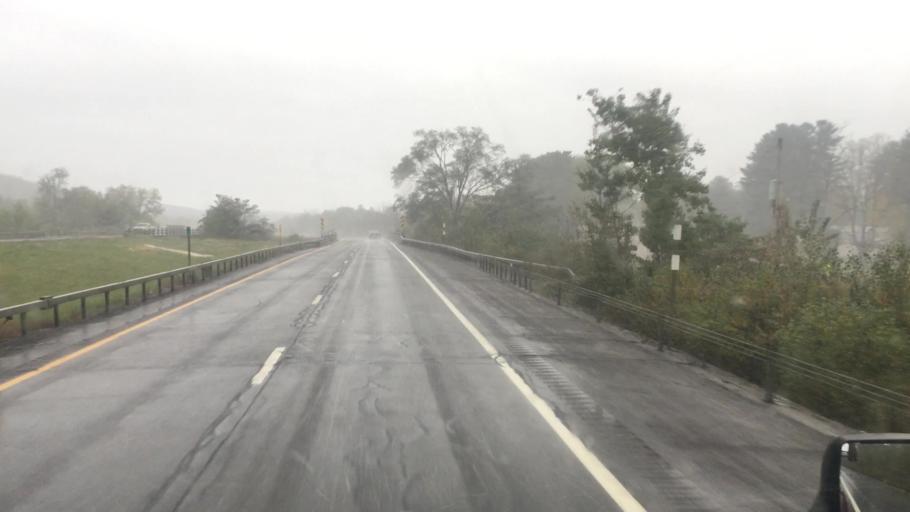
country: US
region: New York
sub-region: Broome County
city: Endicott
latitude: 42.0798
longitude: -76.0765
